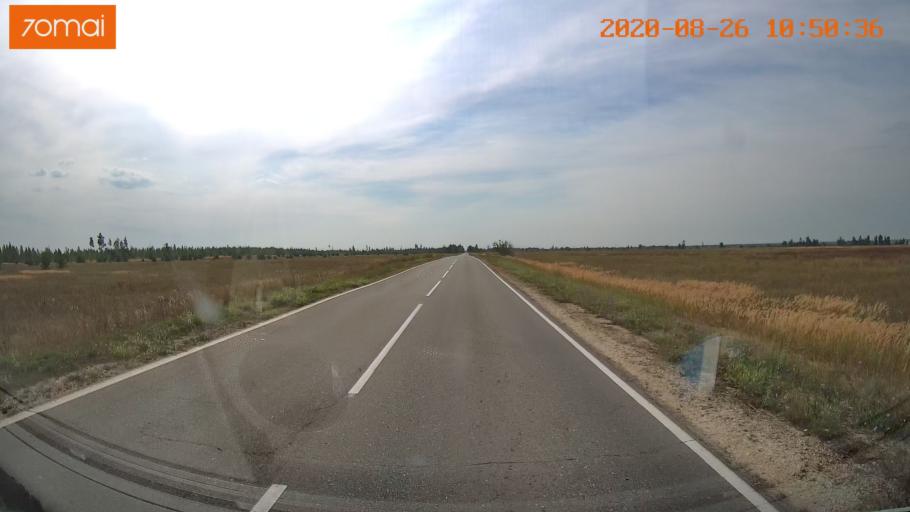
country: RU
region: Rjazan
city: Lashma
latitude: 54.6852
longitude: 41.1563
